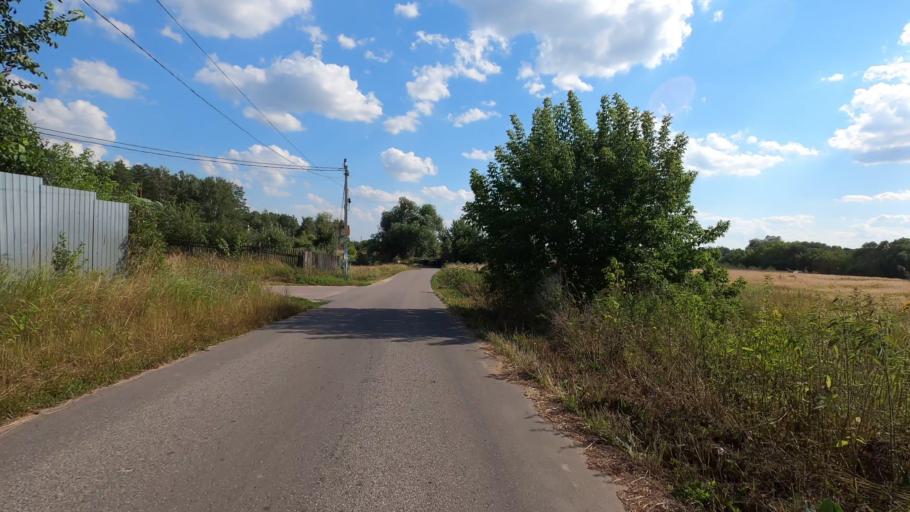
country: RU
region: Moskovskaya
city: Peski
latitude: 55.2108
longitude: 38.7497
